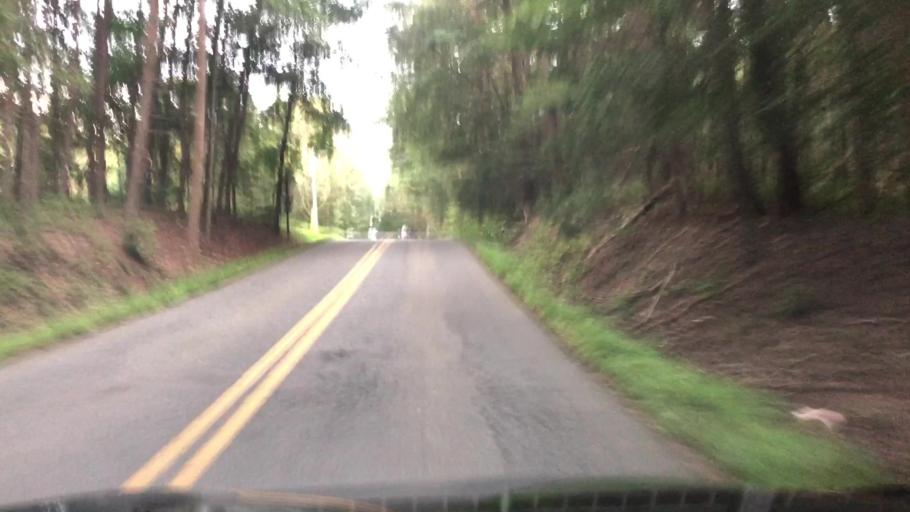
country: US
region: Virginia
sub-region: Fauquier County
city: Bealeton
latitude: 38.5131
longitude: -77.6845
